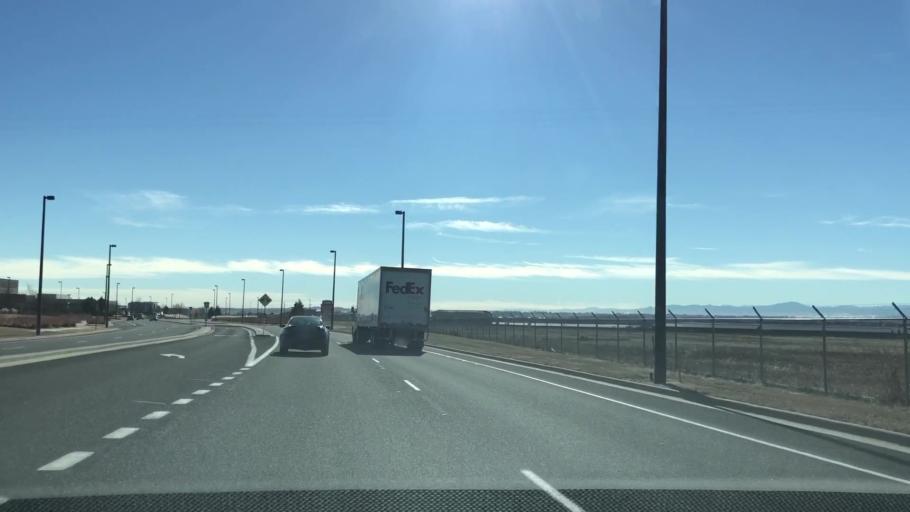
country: US
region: Colorado
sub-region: Larimer County
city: Loveland
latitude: 40.4300
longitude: -104.9989
